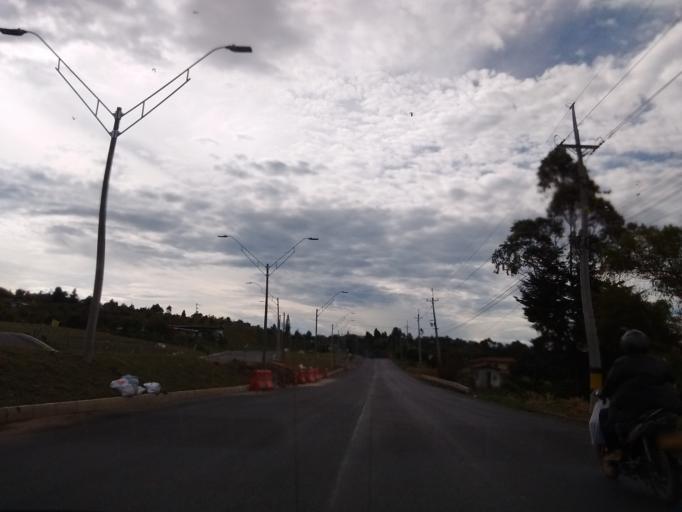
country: CO
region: Antioquia
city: Marinilla
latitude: 6.1443
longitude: -75.3082
